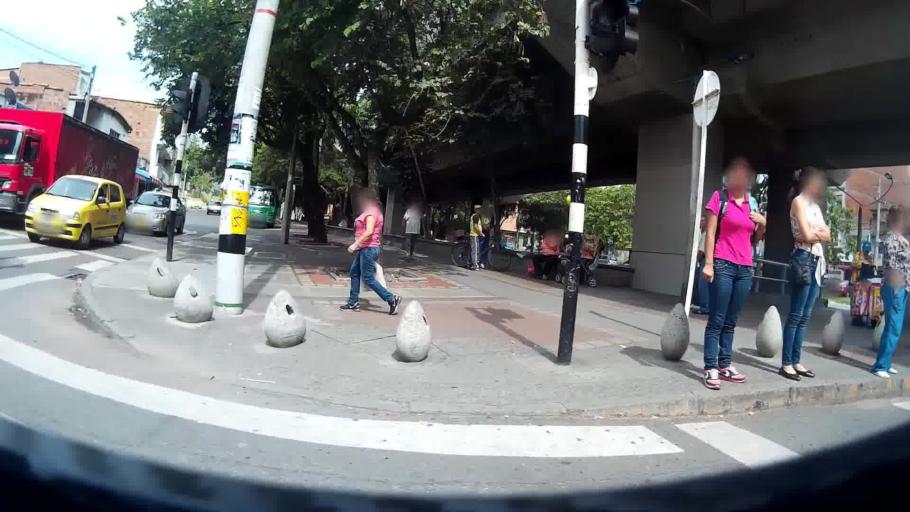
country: CO
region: Antioquia
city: Medellin
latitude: 6.2580
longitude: -75.6036
